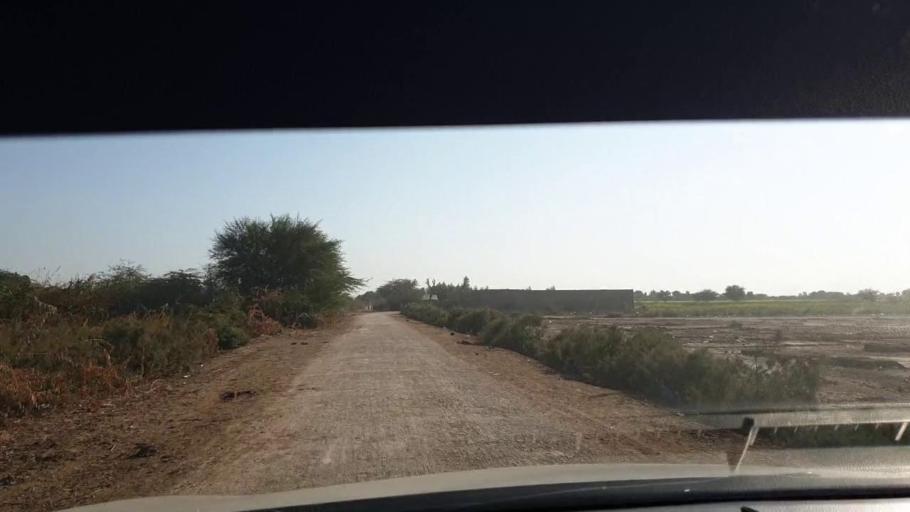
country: PK
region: Sindh
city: Berani
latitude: 25.8094
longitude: 68.9332
